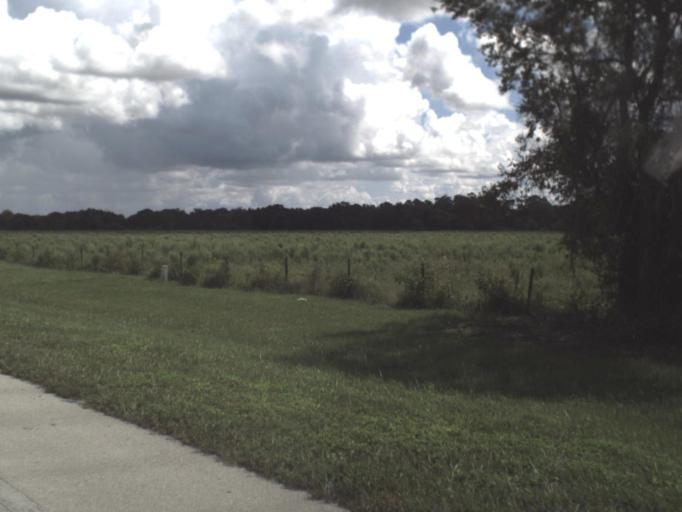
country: US
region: Florida
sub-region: DeSoto County
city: Arcadia
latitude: 27.2088
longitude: -81.8208
